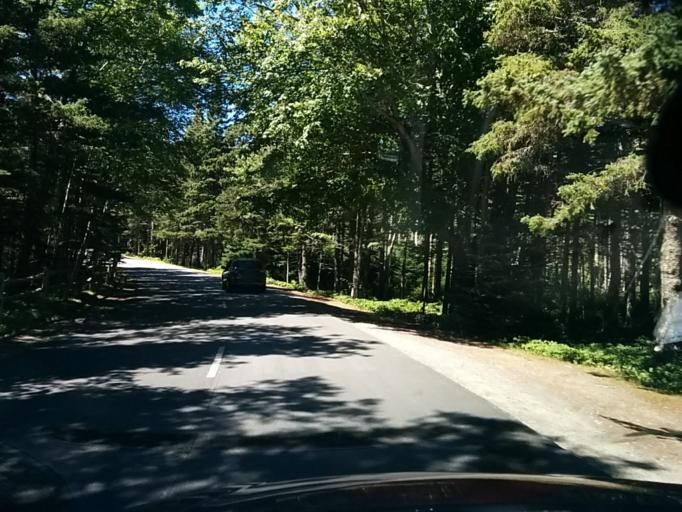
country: US
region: Maine
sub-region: Hancock County
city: Bar Harbor
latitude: 44.2986
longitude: -68.2117
